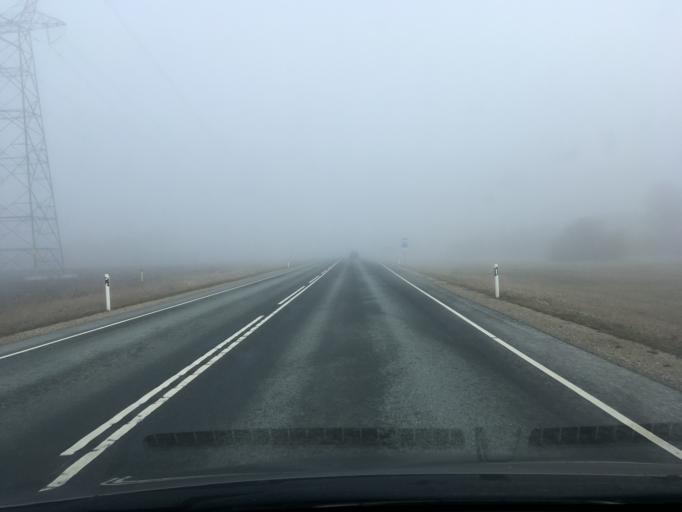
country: EE
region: Harju
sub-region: Nissi vald
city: Turba
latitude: 58.8816
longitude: 24.0886
